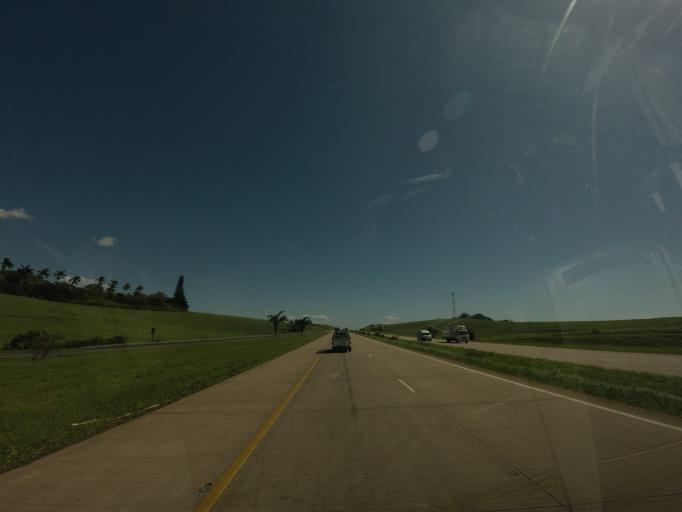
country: ZA
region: KwaZulu-Natal
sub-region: iLembe District Municipality
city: Stanger
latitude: -29.4281
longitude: 31.2731
